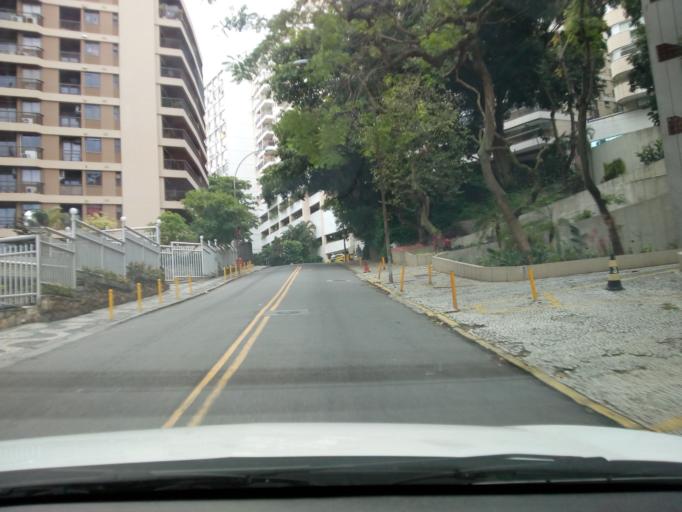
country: BR
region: Rio de Janeiro
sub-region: Rio De Janeiro
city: Rio de Janeiro
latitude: -22.9776
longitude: -43.1973
